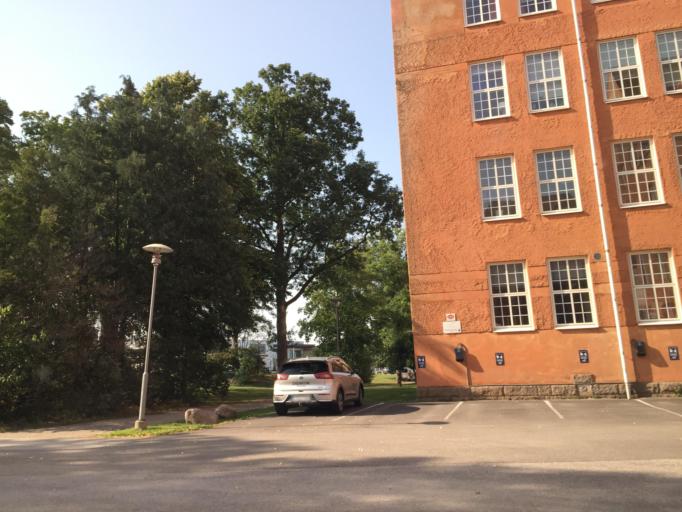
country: SE
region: Vaestra Goetaland
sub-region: Vanersborgs Kommun
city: Vanersborg
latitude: 58.3761
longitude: 12.3343
